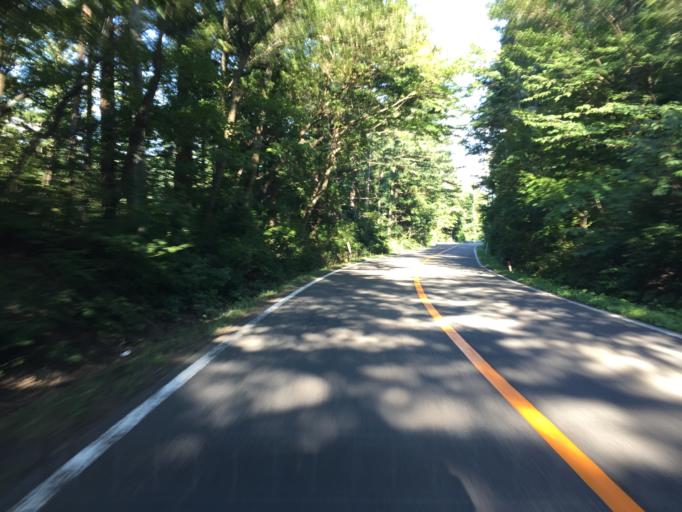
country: JP
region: Miyagi
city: Shiroishi
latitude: 38.0020
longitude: 140.4266
